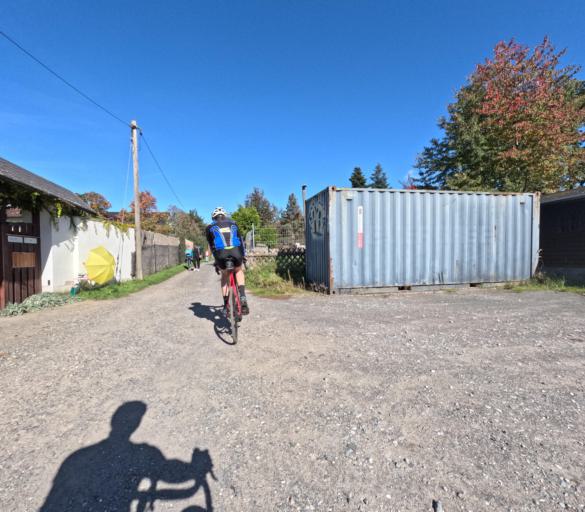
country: DE
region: Saxony
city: Radebeul
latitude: 51.1180
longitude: 13.6643
